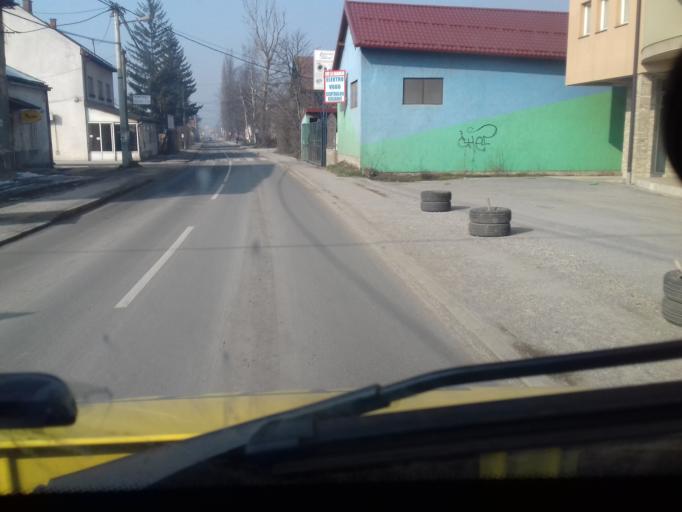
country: BA
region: Federation of Bosnia and Herzegovina
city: Ilijas
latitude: 43.9678
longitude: 18.2577
